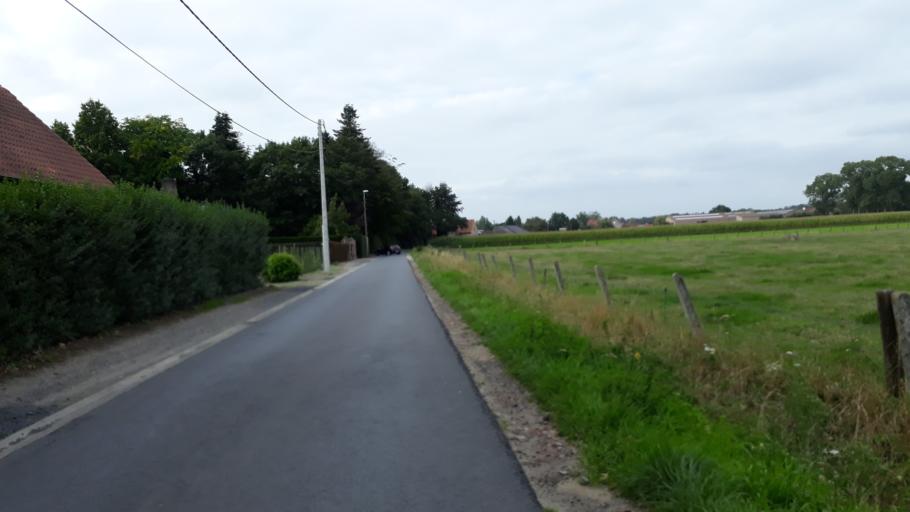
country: BE
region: Flanders
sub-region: Provincie West-Vlaanderen
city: Lichtervelde
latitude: 51.0566
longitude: 3.1361
